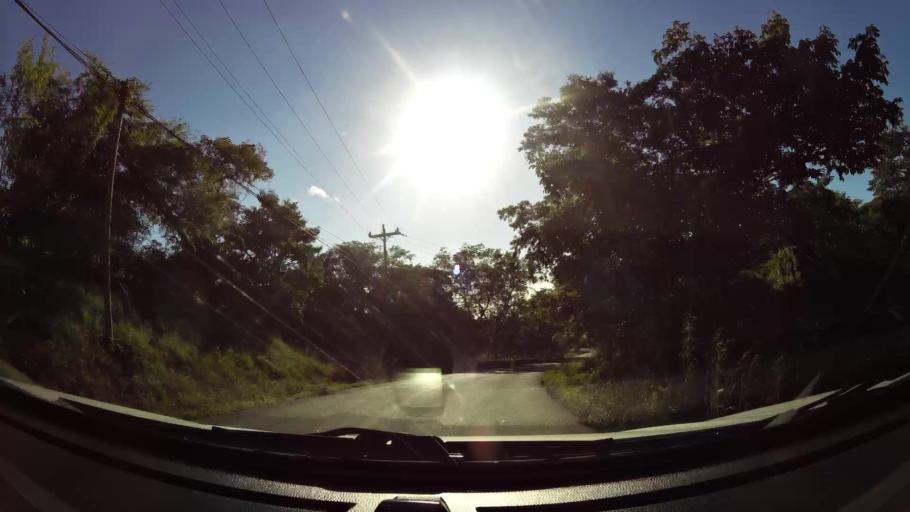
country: CR
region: Guanacaste
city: Sardinal
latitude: 10.4988
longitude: -85.6378
